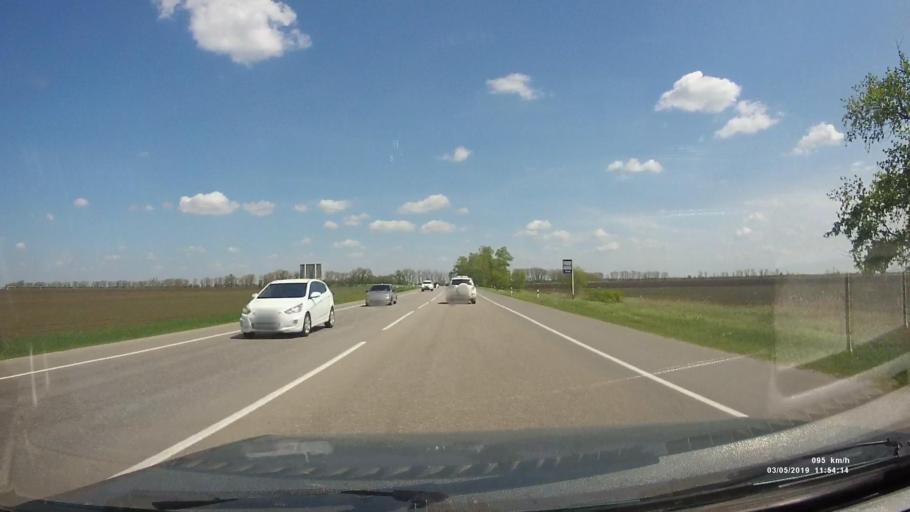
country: RU
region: Rostov
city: Bagayevskaya
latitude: 47.1683
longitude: 40.2796
